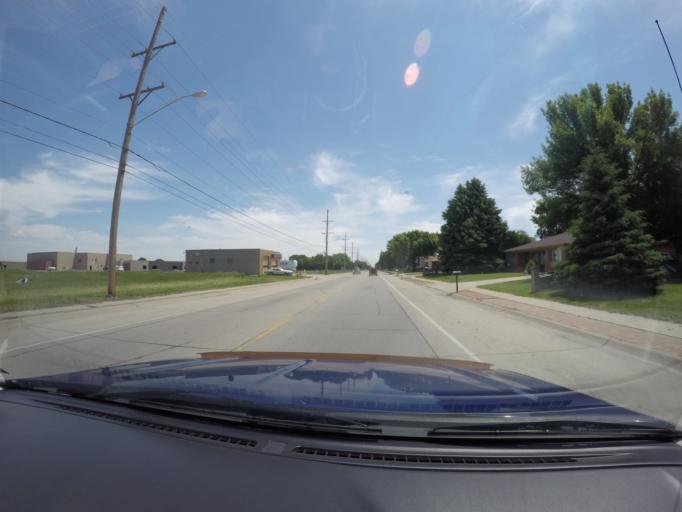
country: US
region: Nebraska
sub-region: Hall County
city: Grand Island
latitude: 40.9022
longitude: -98.3499
